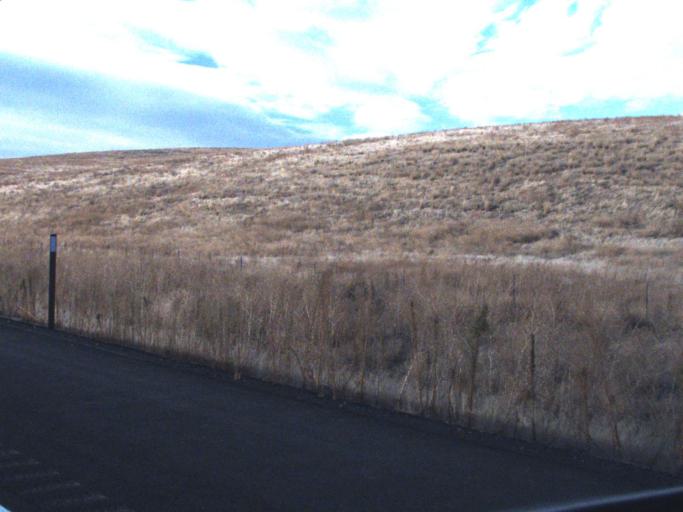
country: US
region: Washington
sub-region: Adams County
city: Ritzville
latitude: 46.9033
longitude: -118.6136
